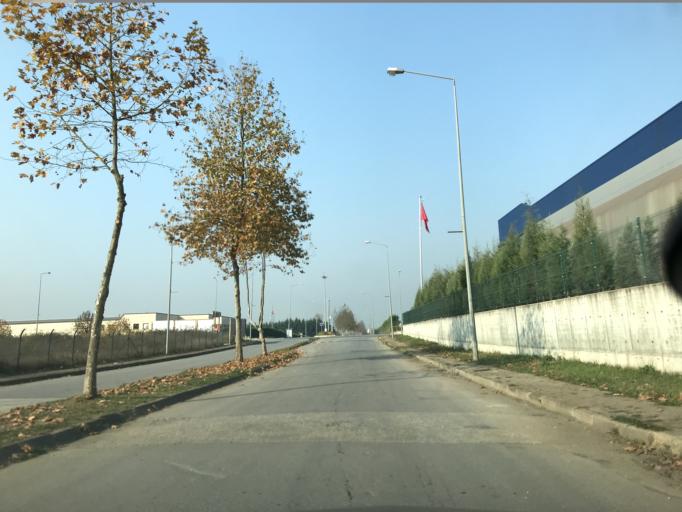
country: TR
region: Duzce
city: Duzce
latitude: 40.7846
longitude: 31.1485
